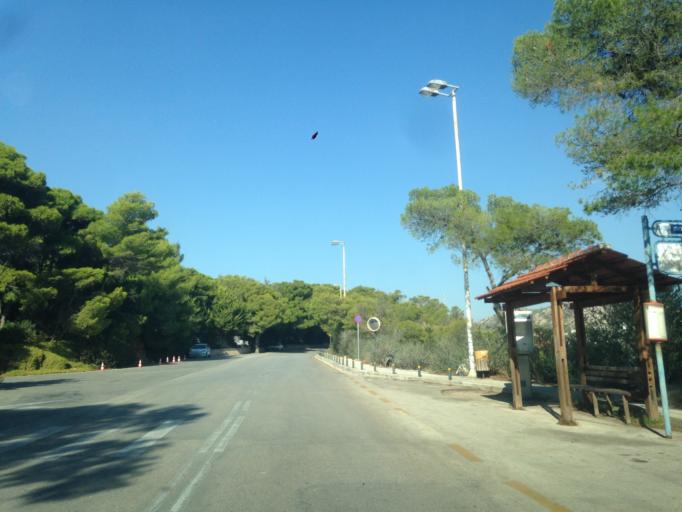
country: GR
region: Attica
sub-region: Nomarchia Anatolikis Attikis
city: Vouliagmeni
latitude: 37.8062
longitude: 23.7737
